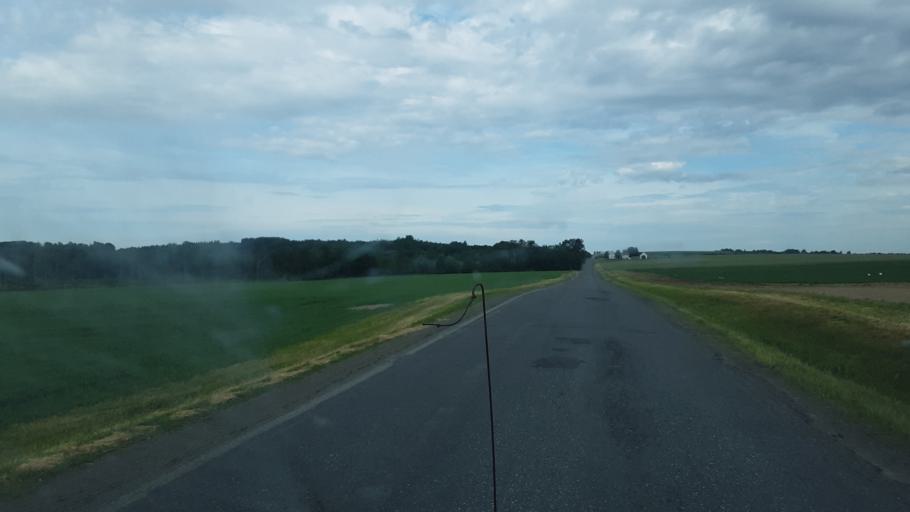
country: US
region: Maine
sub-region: Aroostook County
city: Caribou
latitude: 46.8115
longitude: -68.0032
